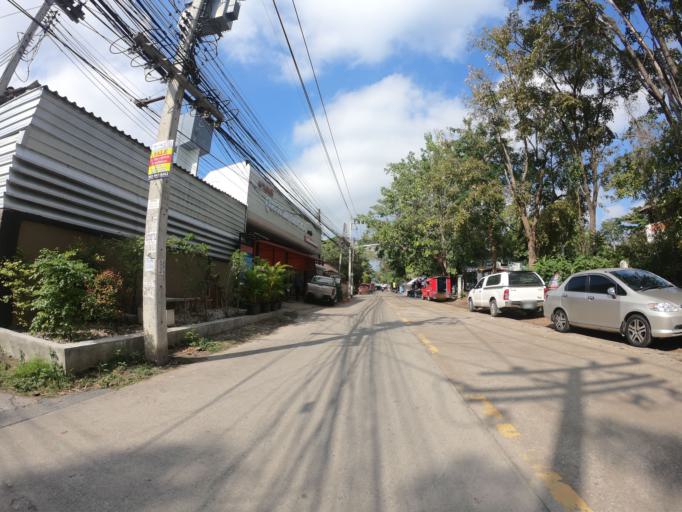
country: TH
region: Chiang Mai
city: Chiang Mai
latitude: 18.7917
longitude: 98.9843
